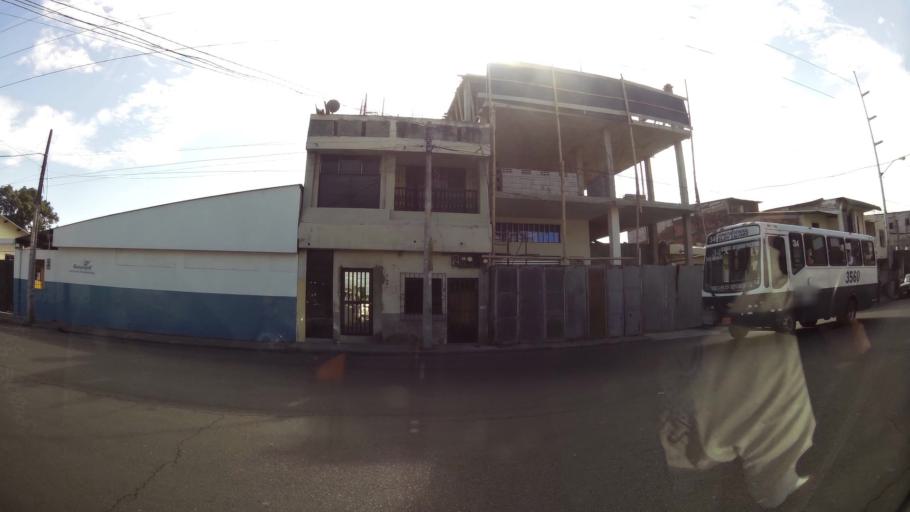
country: EC
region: Guayas
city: Guayaquil
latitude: -2.1960
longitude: -79.9248
